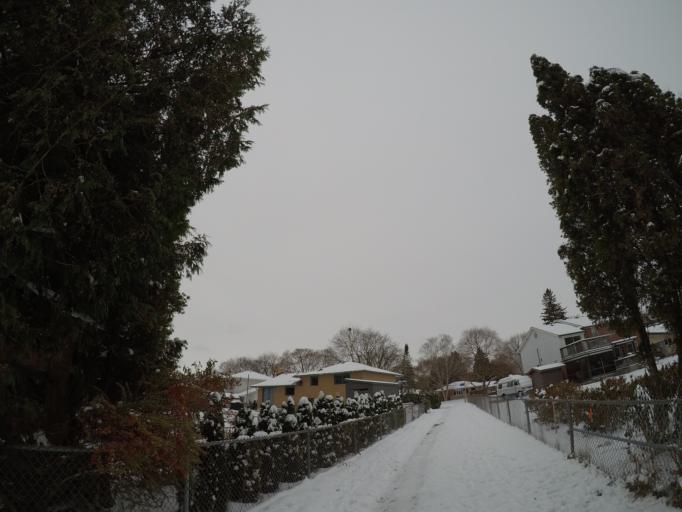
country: CA
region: Ontario
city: Waterloo
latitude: 43.4738
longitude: -80.5127
